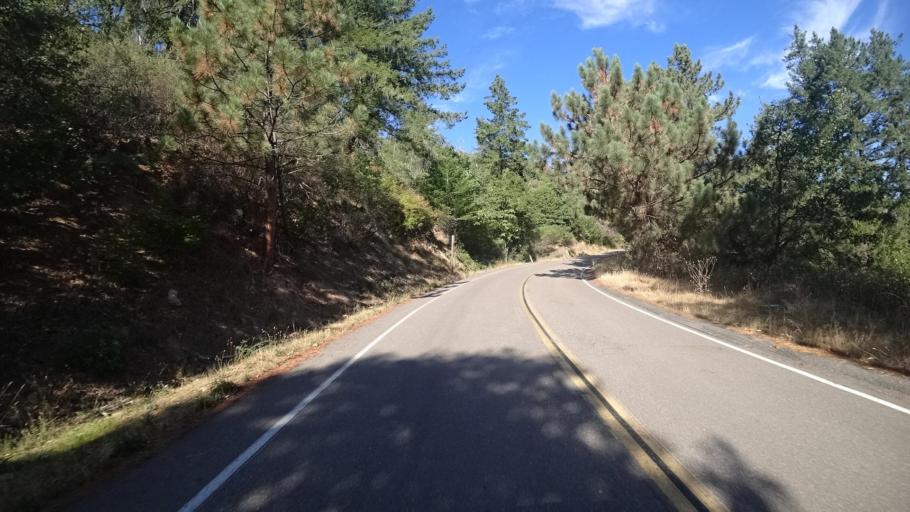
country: US
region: California
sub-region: Riverside County
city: Aguanga
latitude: 33.2859
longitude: -116.7949
